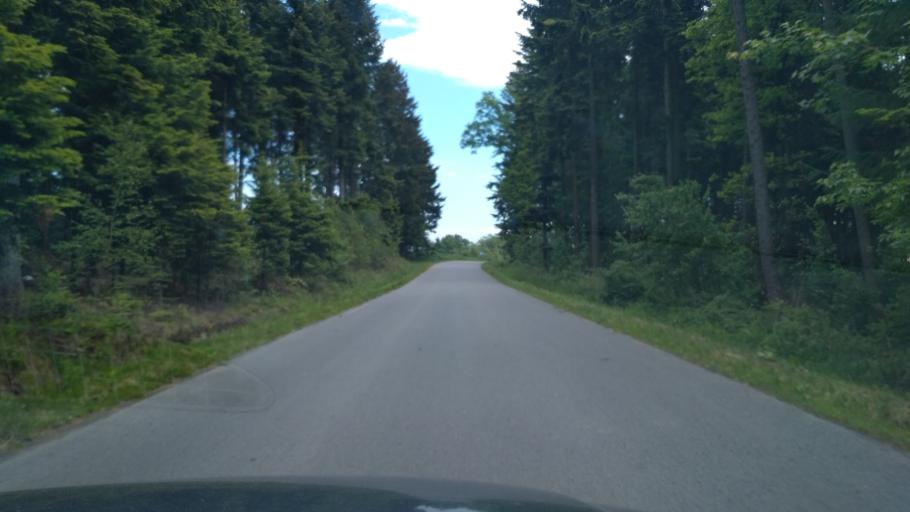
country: PL
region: Subcarpathian Voivodeship
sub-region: Powiat ropczycko-sedziszowski
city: Wielopole Skrzynskie
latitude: 49.9824
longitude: 21.6220
